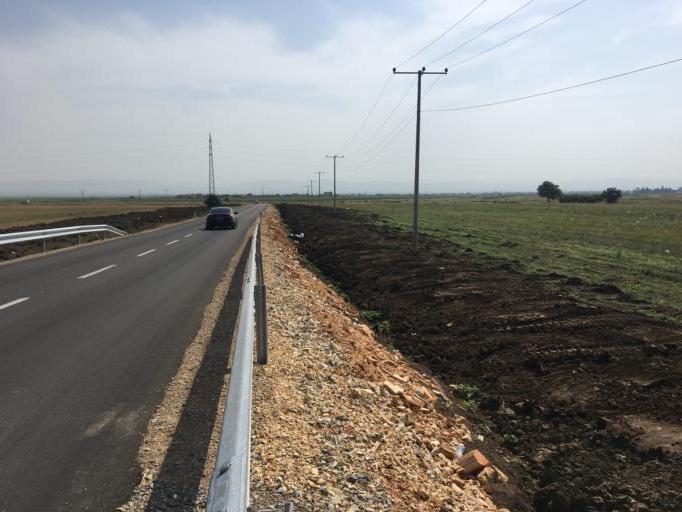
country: XK
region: Pristina
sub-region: Komuna e Gracanices
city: Glanica
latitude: 42.5440
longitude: 21.0175
